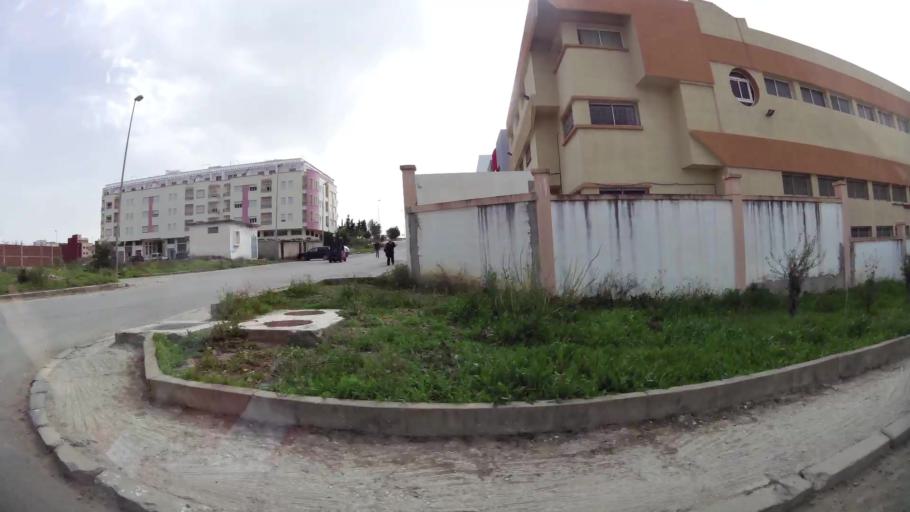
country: MA
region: Tanger-Tetouan
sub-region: Tanger-Assilah
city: Boukhalef
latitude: 35.7126
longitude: -5.8951
